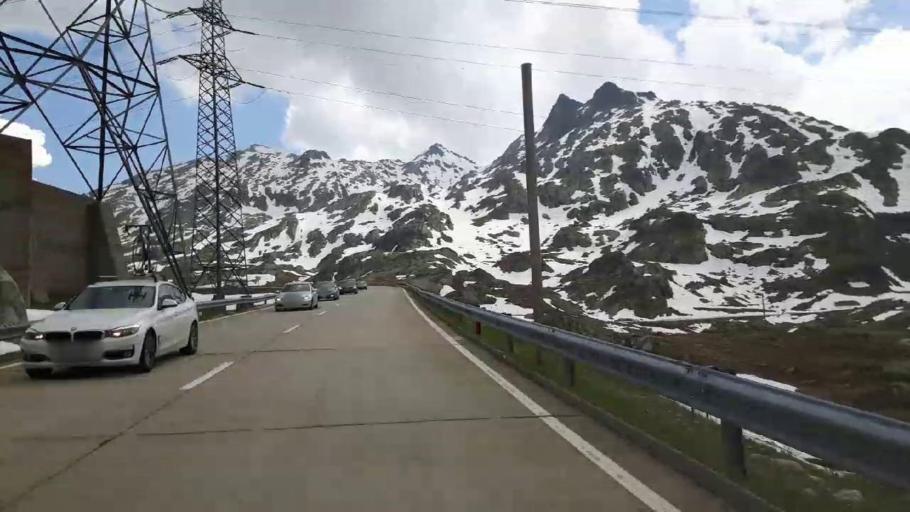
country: CH
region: Ticino
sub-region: Leventina District
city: Airolo
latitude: 46.5636
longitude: 8.5601
